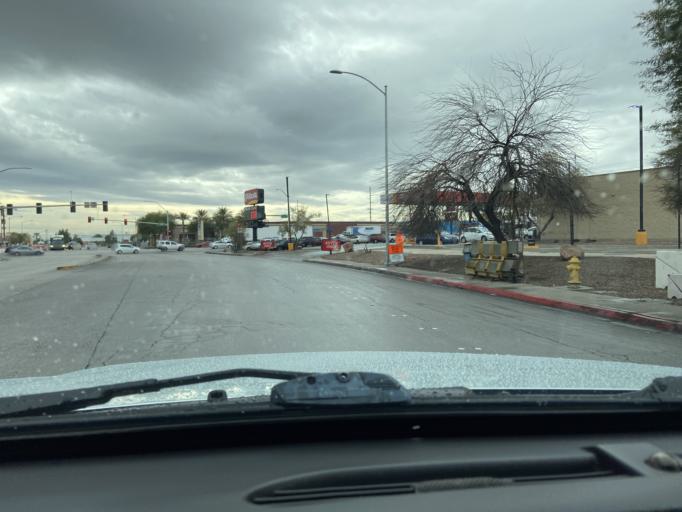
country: US
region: Nevada
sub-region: Clark County
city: Sunrise Manor
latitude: 36.2412
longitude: -115.0972
